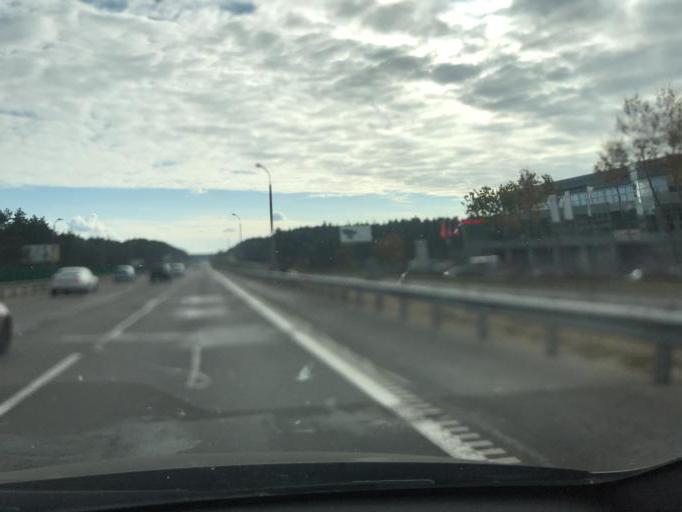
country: BY
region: Minsk
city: Vyaliki Trastsyanets
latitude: 53.9056
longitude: 27.6874
